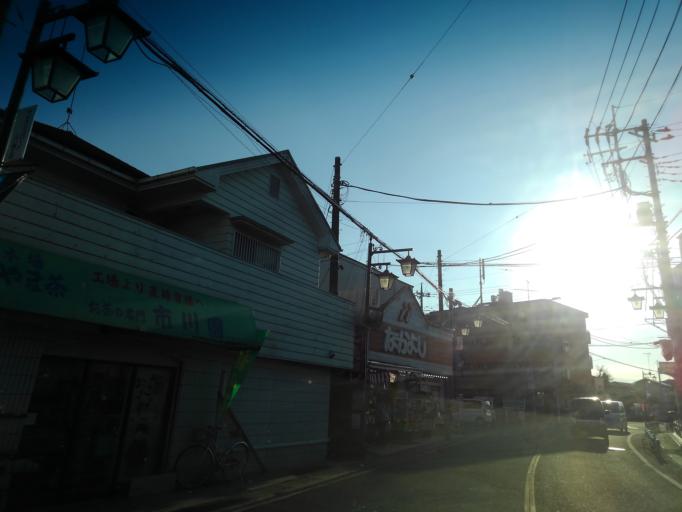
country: JP
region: Saitama
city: Tokorozawa
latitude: 35.7795
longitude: 139.4403
